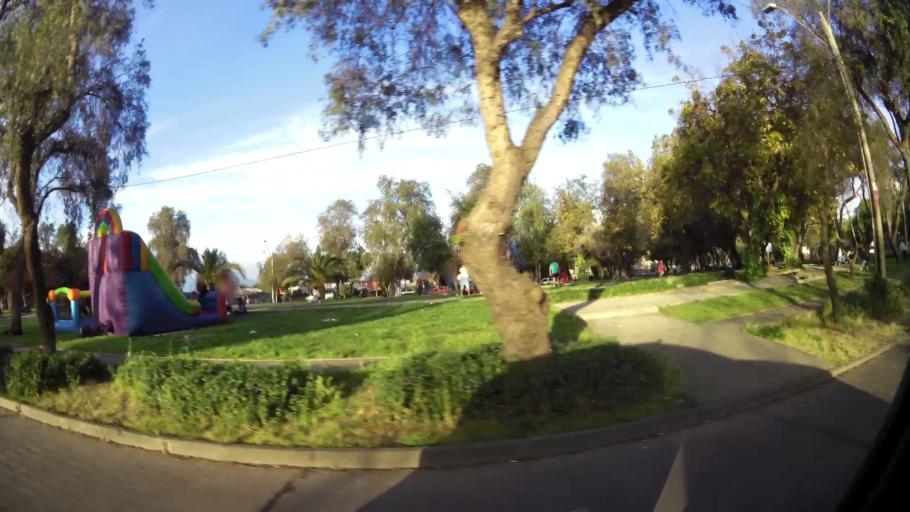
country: CL
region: Santiago Metropolitan
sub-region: Provincia de Santiago
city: Lo Prado
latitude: -33.4554
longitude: -70.7226
